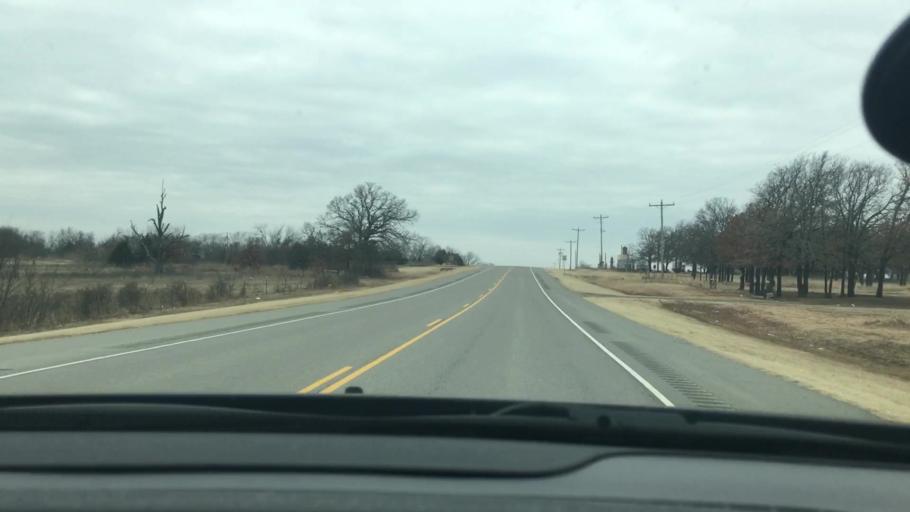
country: US
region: Oklahoma
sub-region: Carter County
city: Healdton
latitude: 34.4880
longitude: -97.4514
